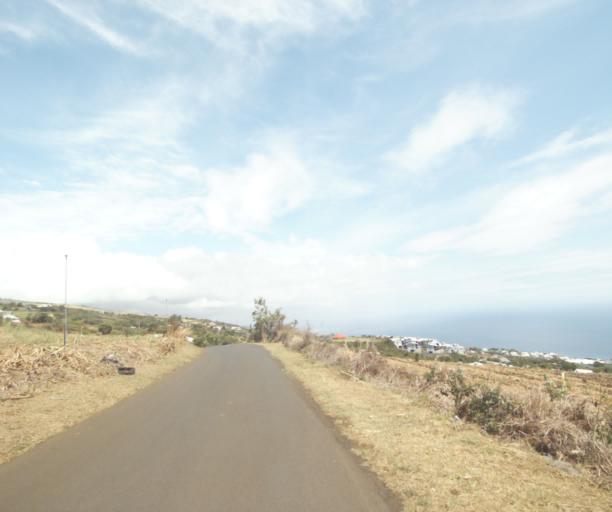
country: RE
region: Reunion
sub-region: Reunion
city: Trois-Bassins
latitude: -21.0935
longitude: 55.2758
